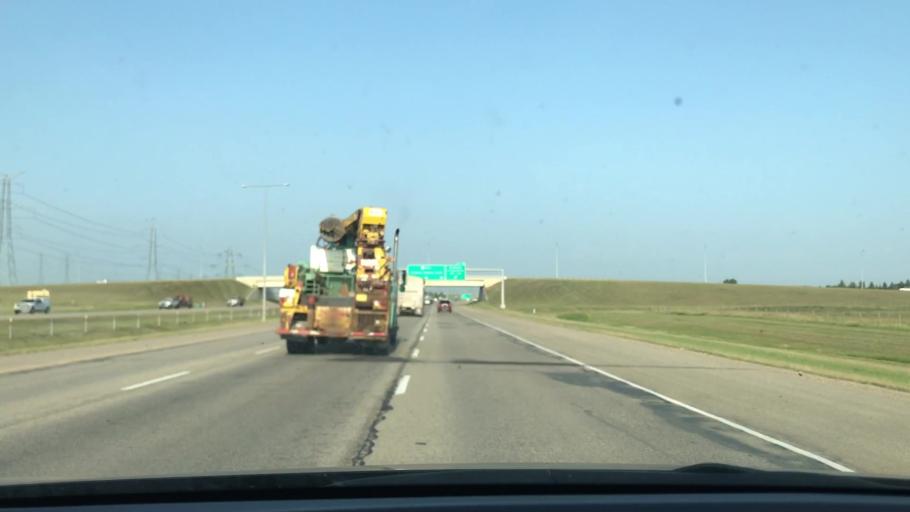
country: CA
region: Alberta
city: Beaumont
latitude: 53.4359
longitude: -113.4366
